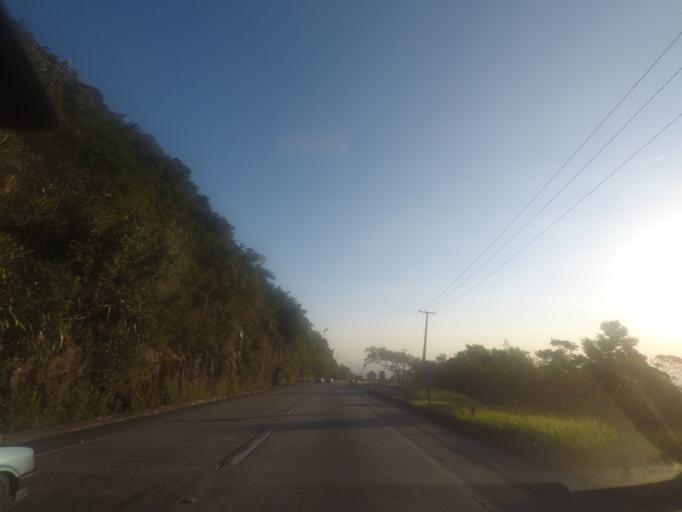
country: BR
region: Rio de Janeiro
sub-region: Petropolis
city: Petropolis
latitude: -22.5284
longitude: -43.2349
